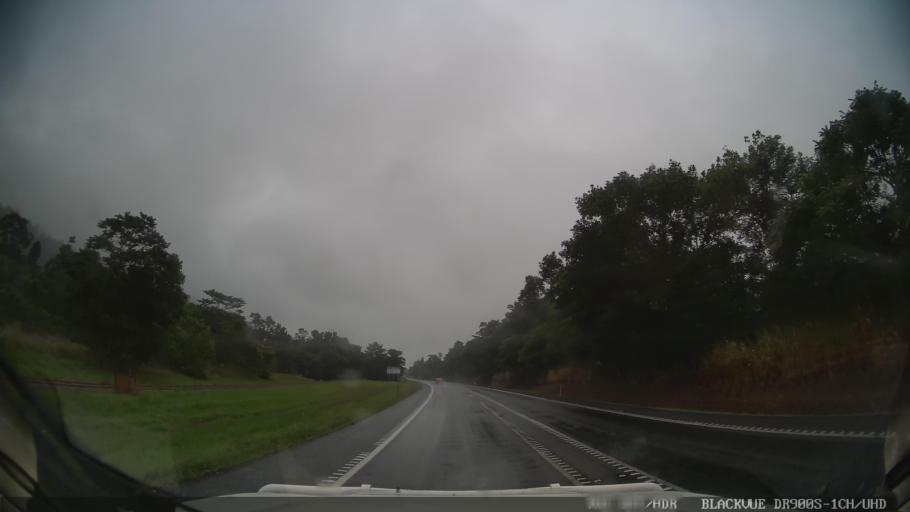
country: AU
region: Queensland
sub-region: Cassowary Coast
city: Innisfail
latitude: -17.8590
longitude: 145.9867
